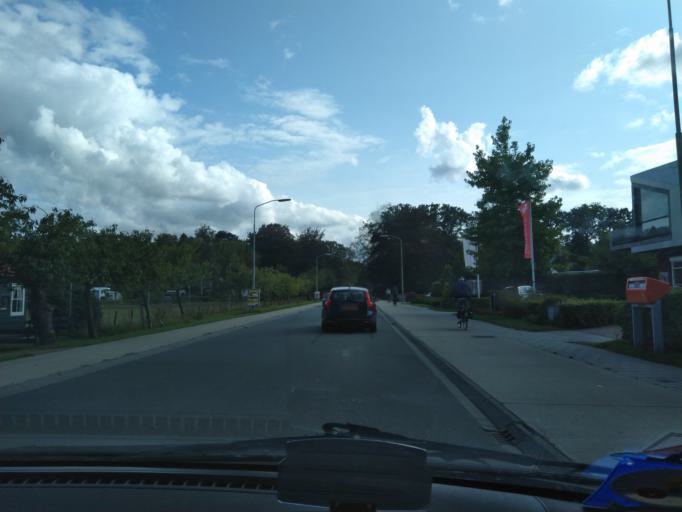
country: NL
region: Groningen
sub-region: Gemeente Haren
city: Haren
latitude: 53.1561
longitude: 6.5642
